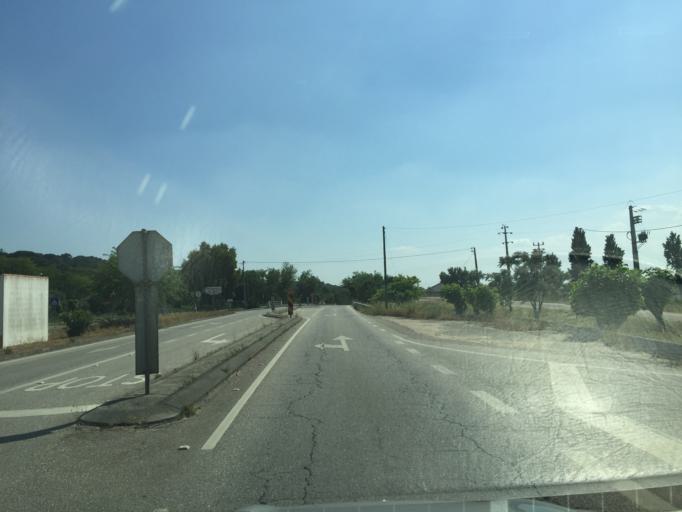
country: PT
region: Santarem
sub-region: Golega
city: Golega
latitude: 39.3932
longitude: -8.4401
